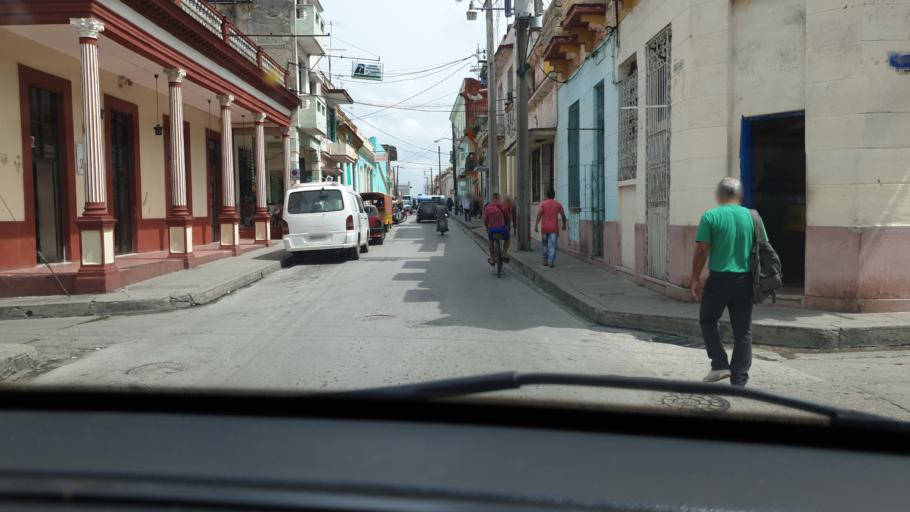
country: CU
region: Villa Clara
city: Santa Clara
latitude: 22.4060
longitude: -79.9668
